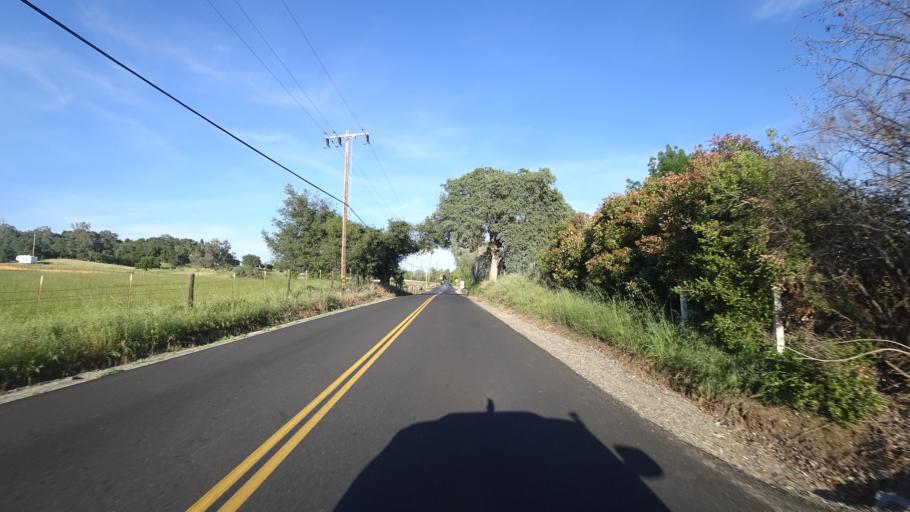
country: US
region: California
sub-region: Placer County
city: Lincoln
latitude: 38.9123
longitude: -121.2184
